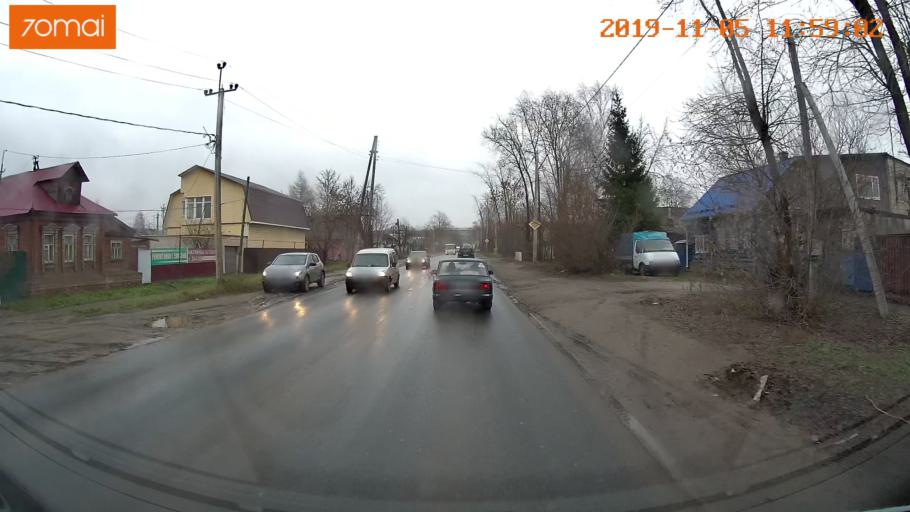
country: RU
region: Ivanovo
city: Kokhma
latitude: 56.9794
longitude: 41.0446
